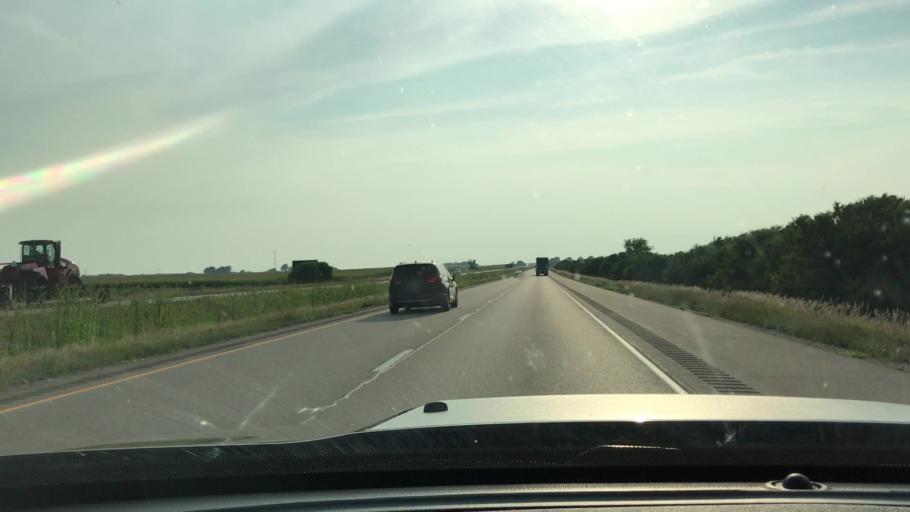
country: US
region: Illinois
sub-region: Bureau County
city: Princeton
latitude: 41.3946
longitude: -89.6007
